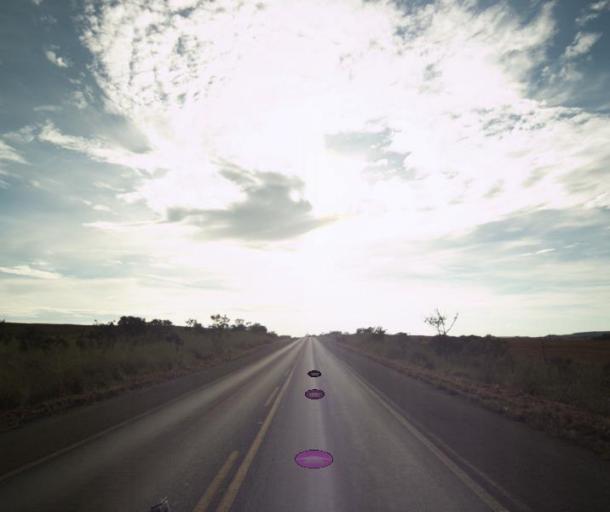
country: BR
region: Goias
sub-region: Pirenopolis
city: Pirenopolis
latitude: -15.7633
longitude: -48.6998
